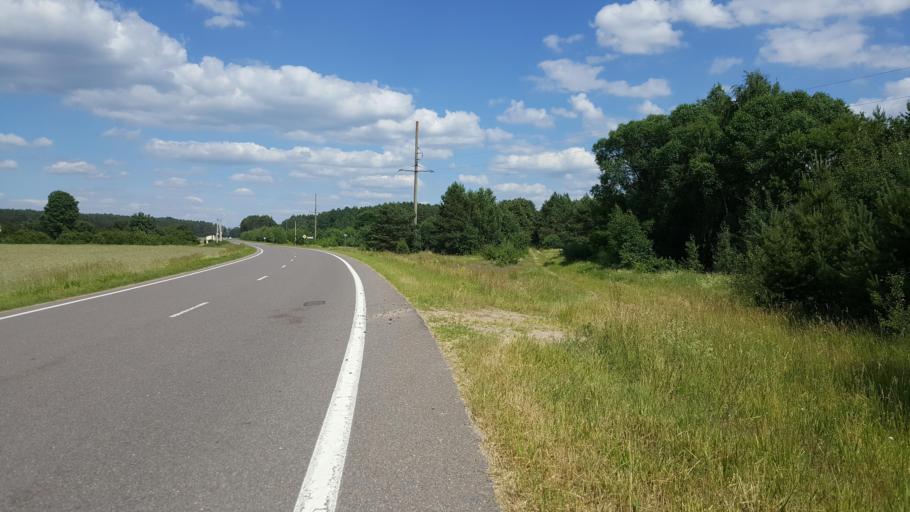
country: BY
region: Brest
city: Kamyanyuki
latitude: 52.5032
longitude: 23.6885
